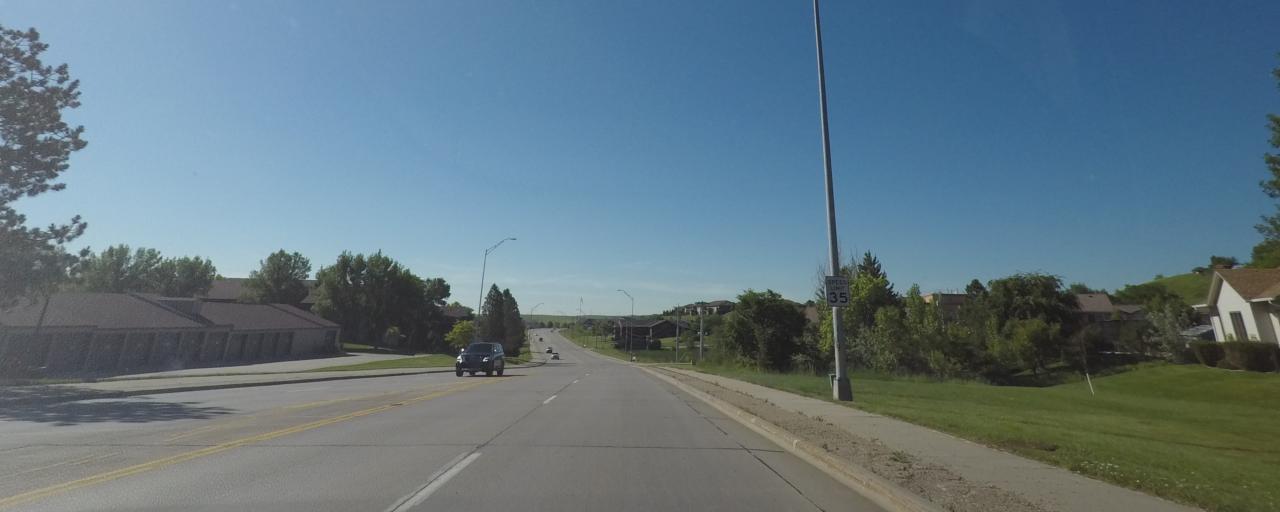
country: US
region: South Dakota
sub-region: Pennington County
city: Rapid City
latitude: 44.0489
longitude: -103.2235
